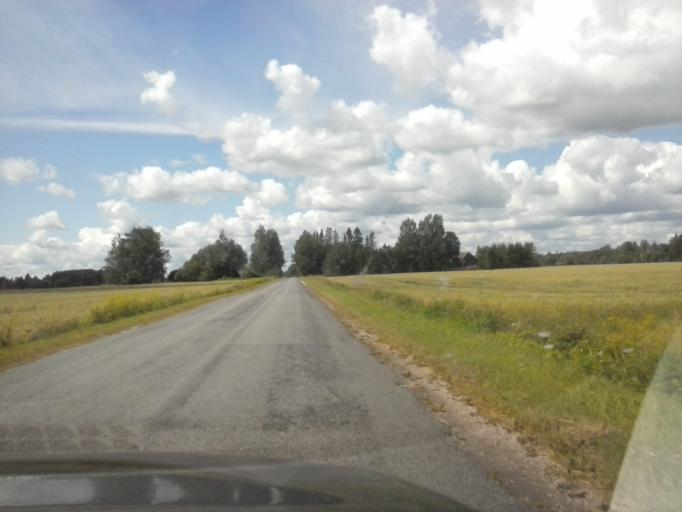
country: EE
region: Laeaene-Virumaa
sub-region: Rakke vald
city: Rakke
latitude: 59.0508
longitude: 26.3694
